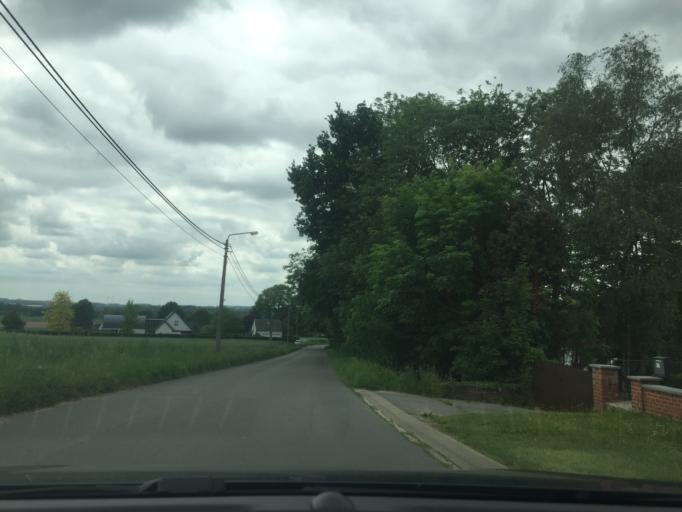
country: BE
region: Wallonia
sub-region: Province du Hainaut
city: Tournai
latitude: 50.6463
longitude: 3.4034
